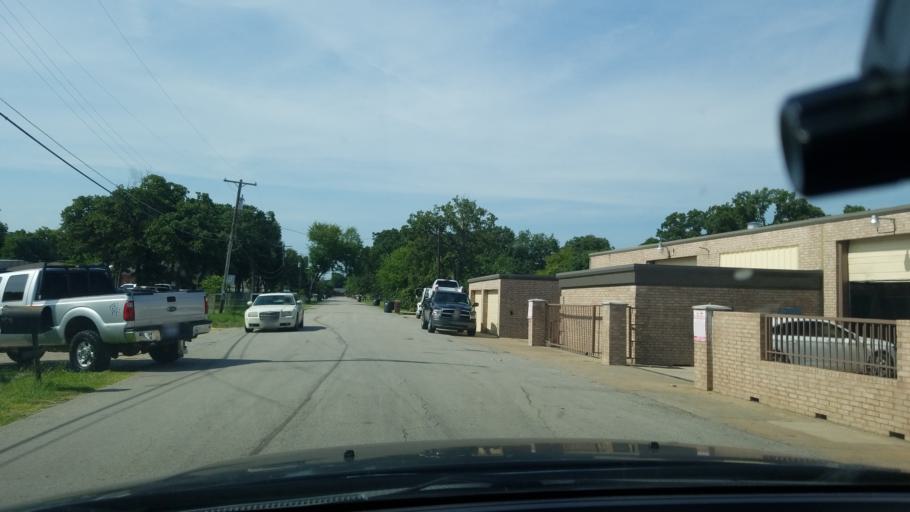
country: US
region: Texas
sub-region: Dallas County
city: Balch Springs
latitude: 32.7338
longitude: -96.6367
